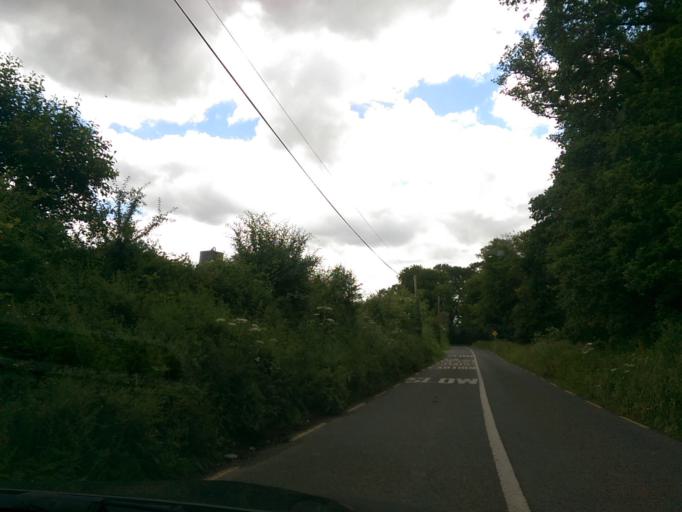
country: IE
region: Munster
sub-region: North Tipperary
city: Nenagh
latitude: 52.8095
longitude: -8.1940
